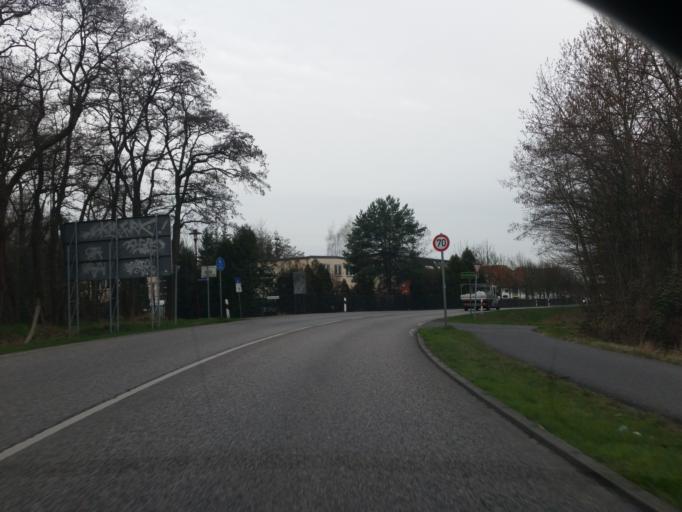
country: DE
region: Brandenburg
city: Grossbeeren
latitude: 52.3832
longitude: 13.3168
